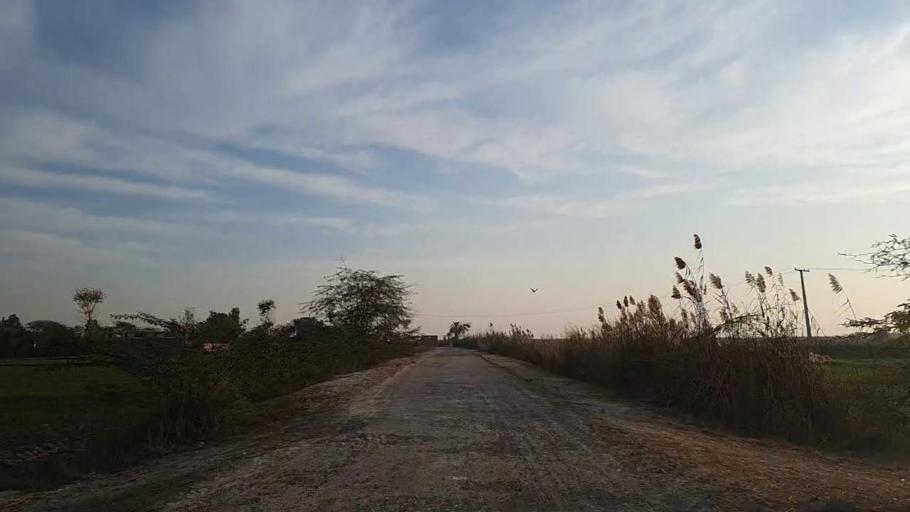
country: PK
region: Sindh
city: Bandhi
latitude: 26.5852
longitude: 68.3332
